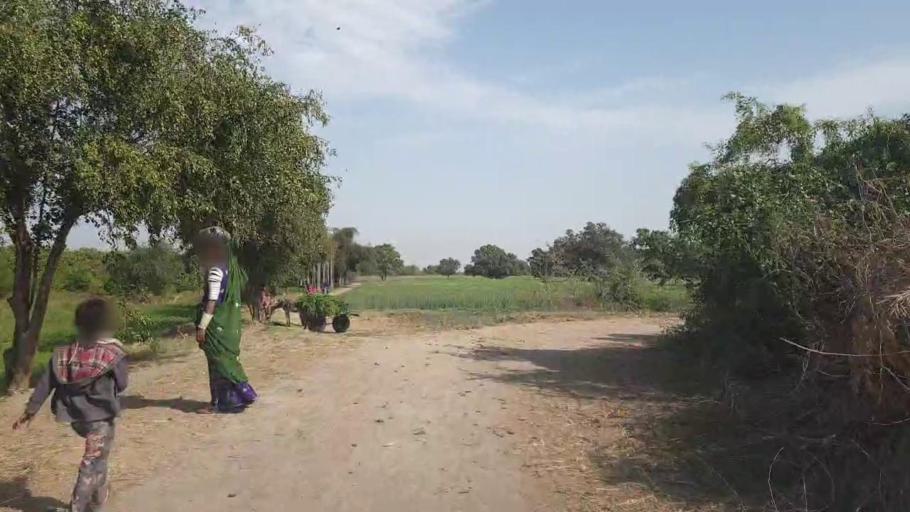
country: PK
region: Sindh
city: Dhoro Naro
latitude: 25.4502
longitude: 69.5398
